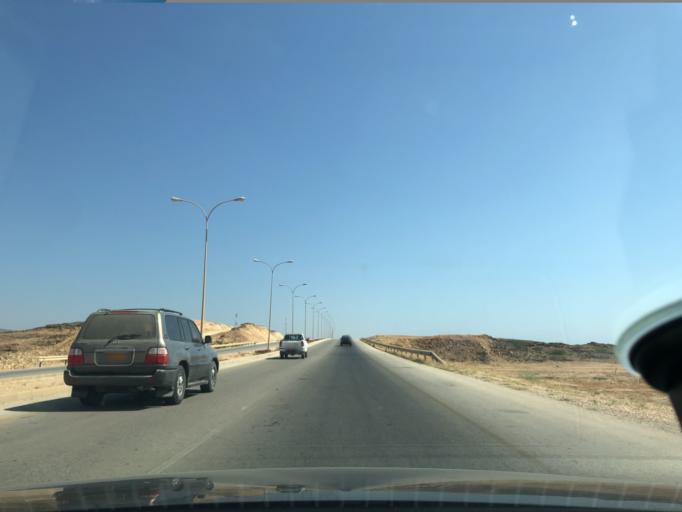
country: OM
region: Zufar
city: Salalah
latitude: 17.0513
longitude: 54.3119
